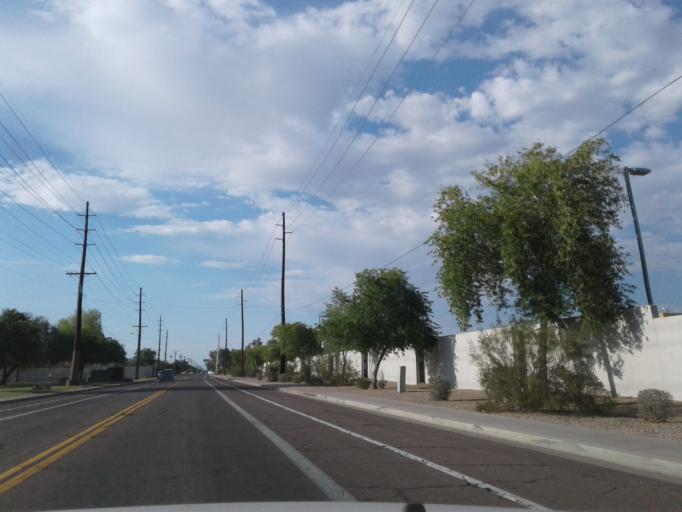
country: US
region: Arizona
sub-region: Maricopa County
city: Tempe
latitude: 33.4485
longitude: -111.9180
